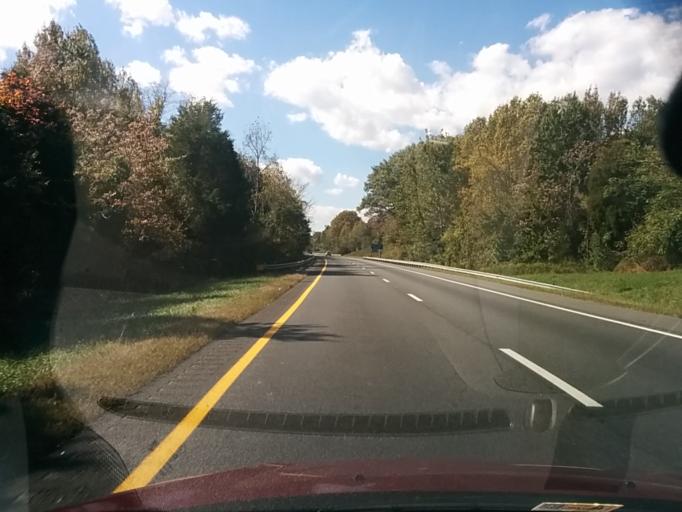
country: US
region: Virginia
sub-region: Albemarle County
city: Crozet
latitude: 38.0359
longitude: -78.6146
